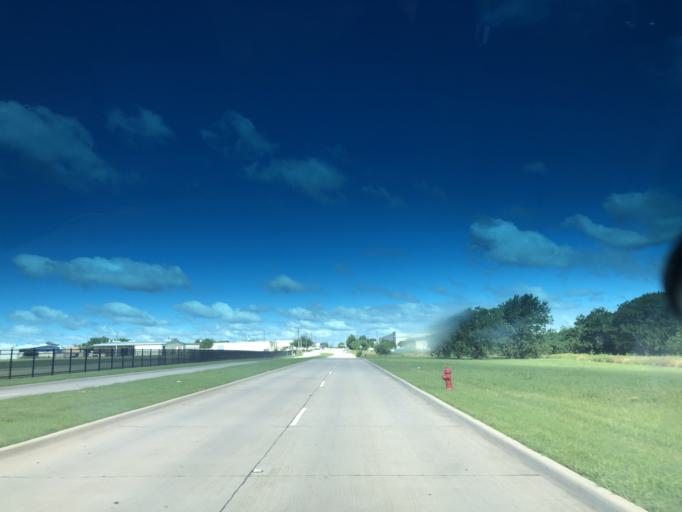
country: US
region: Texas
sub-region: Dallas County
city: Grand Prairie
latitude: 32.7061
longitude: -97.0459
